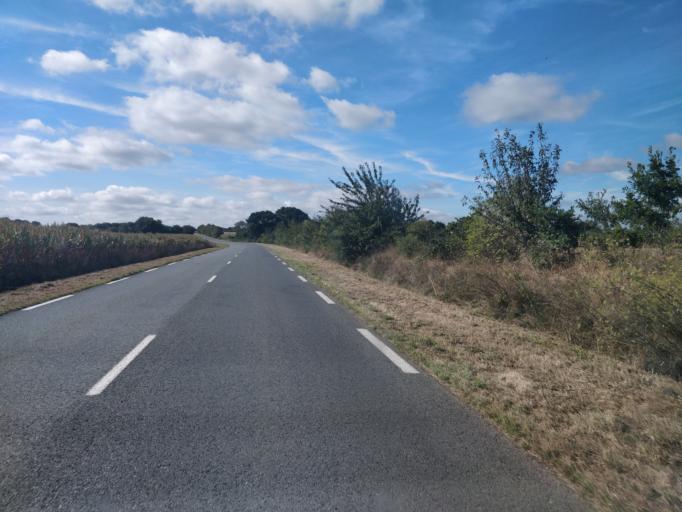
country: FR
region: Brittany
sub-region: Departement des Cotes-d'Armor
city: Erquy
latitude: 48.6068
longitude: -2.4684
